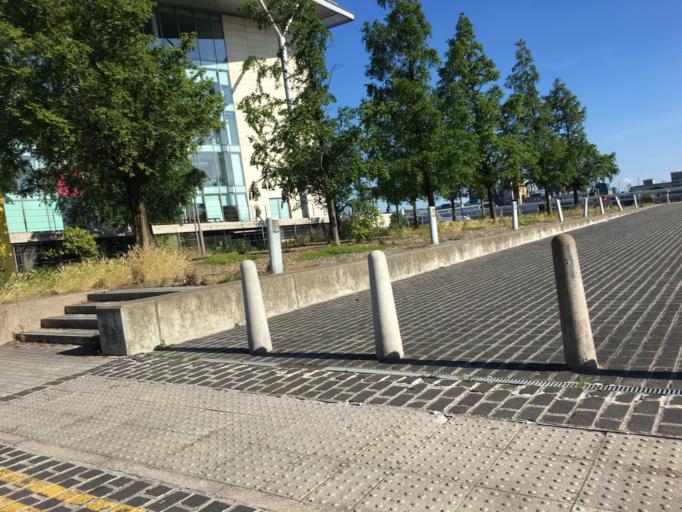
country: GB
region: England
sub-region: Greater London
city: East Ham
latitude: 51.5081
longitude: 0.0455
